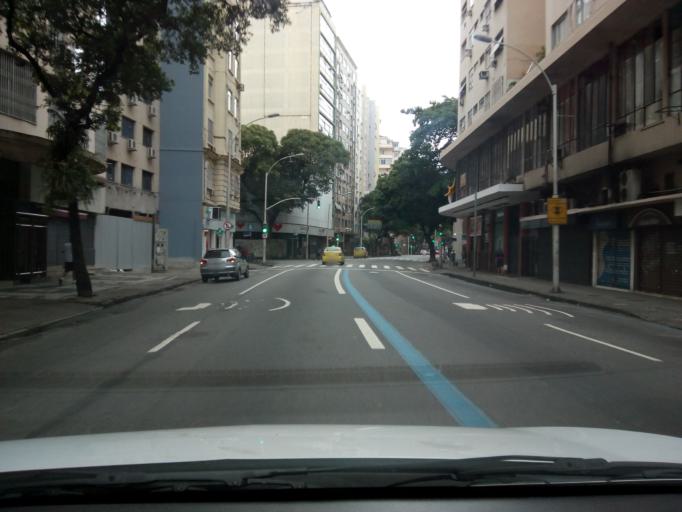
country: BR
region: Rio de Janeiro
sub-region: Rio De Janeiro
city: Rio de Janeiro
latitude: -22.9765
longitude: -43.1903
